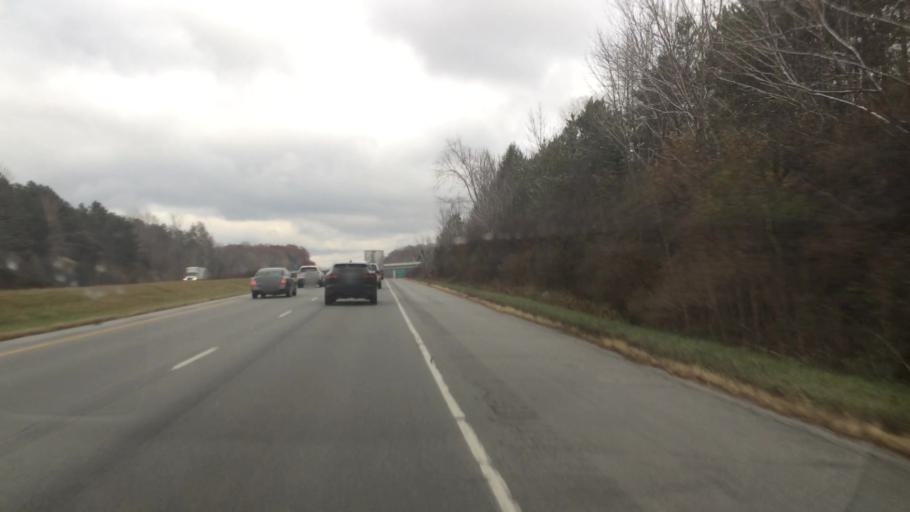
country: US
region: Ohio
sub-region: Summit County
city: Hudson
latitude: 41.2721
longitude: -81.4037
